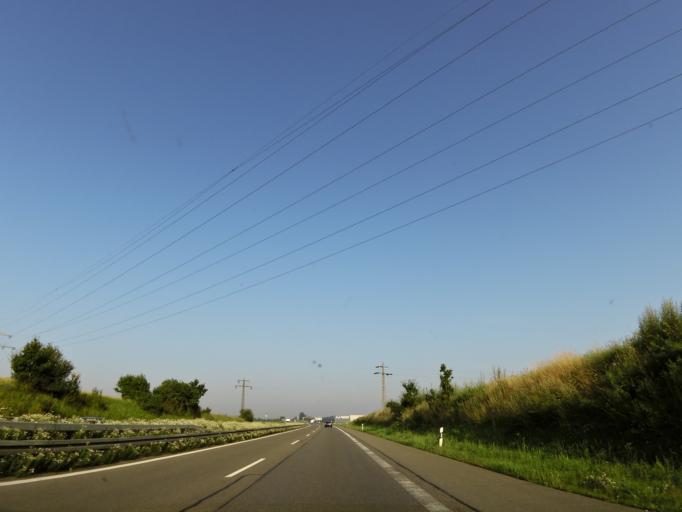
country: DE
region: Baden-Wuerttemberg
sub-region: Tuebingen Region
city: Beimerstetten
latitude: 48.4580
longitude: 9.9916
